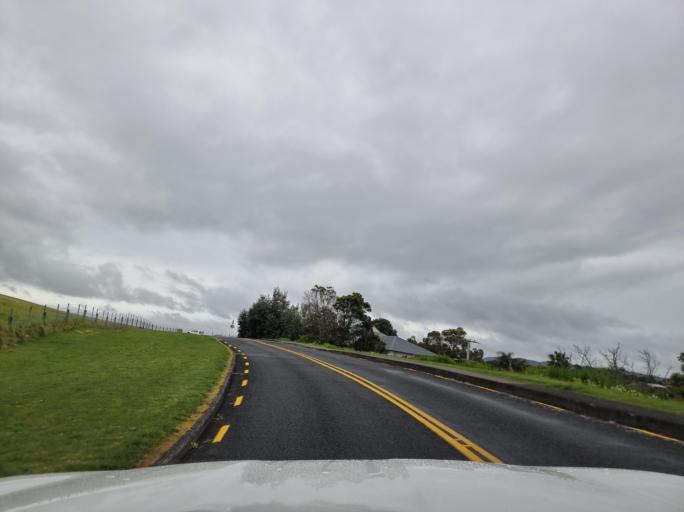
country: NZ
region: Northland
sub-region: Whangarei
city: Whangarei
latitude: -35.7677
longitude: 174.3704
